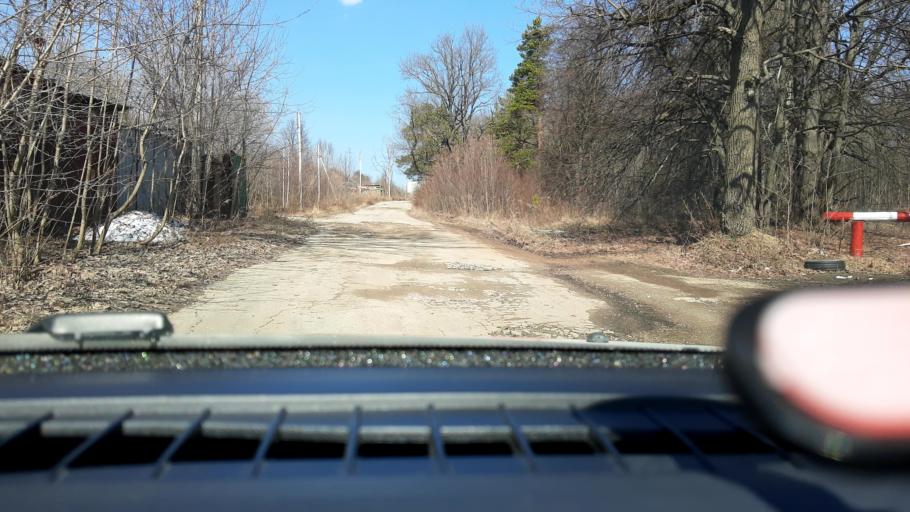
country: RU
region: Nizjnij Novgorod
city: Nizhniy Novgorod
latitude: 56.2512
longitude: 44.0023
